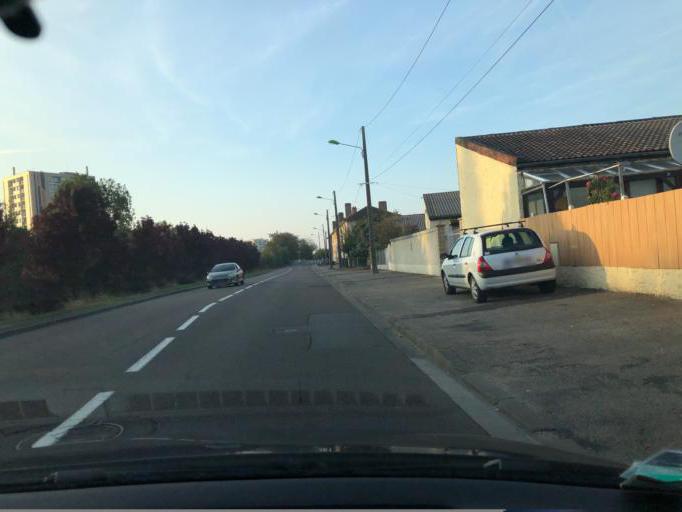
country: FR
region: Bourgogne
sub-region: Departement de l'Yonne
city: Saint-Clement
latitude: 48.2006
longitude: 3.3008
